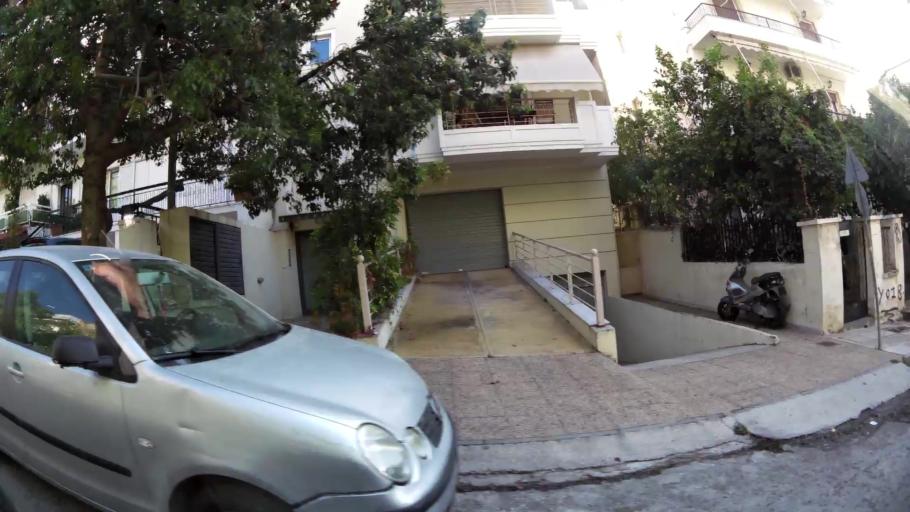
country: GR
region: Attica
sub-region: Nomarchia Athinas
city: Ilioupoli
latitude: 37.9443
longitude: 23.7694
